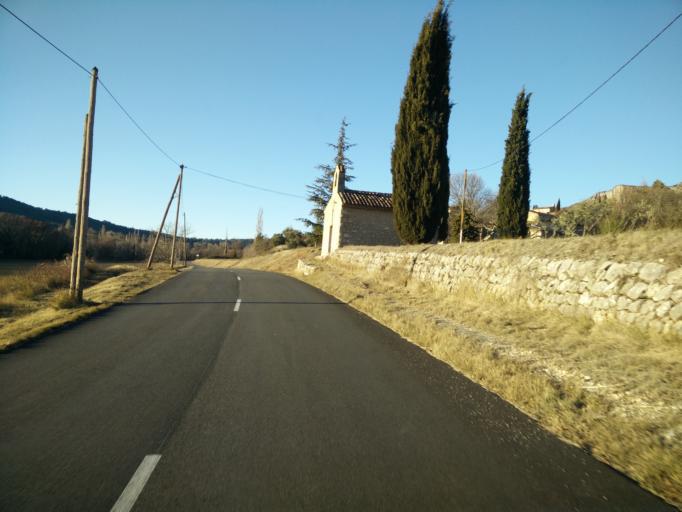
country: FR
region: Provence-Alpes-Cote d'Azur
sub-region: Departement des Alpes-de-Haute-Provence
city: Riez
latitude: 43.8312
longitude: 6.2248
